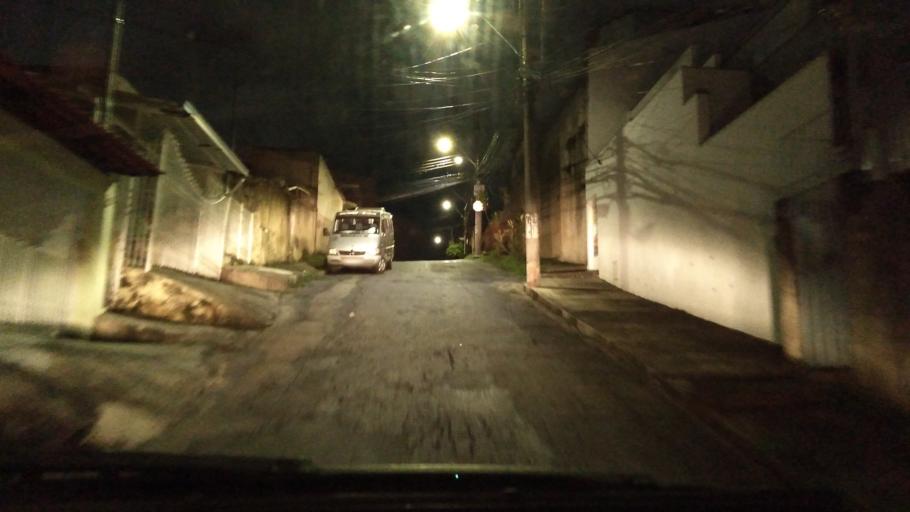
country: BR
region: Minas Gerais
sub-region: Belo Horizonte
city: Belo Horizonte
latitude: -19.8996
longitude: -43.9732
